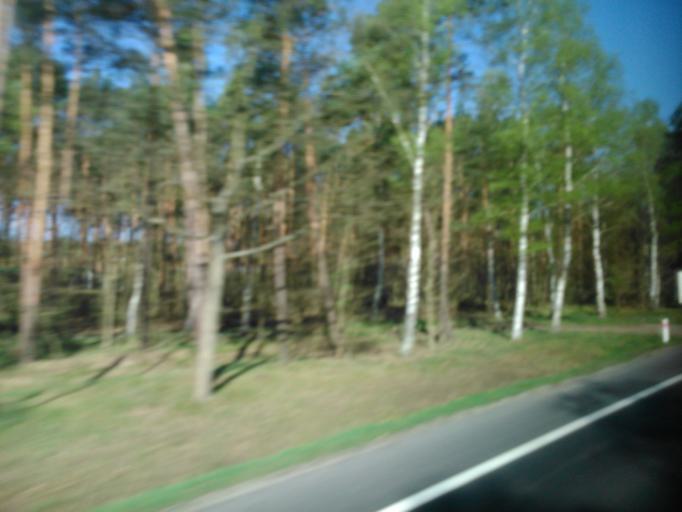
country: PL
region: Kujawsko-Pomorskie
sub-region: Powiat aleksandrowski
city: Aleksandrow Kujawski
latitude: 52.8912
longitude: 18.7316
